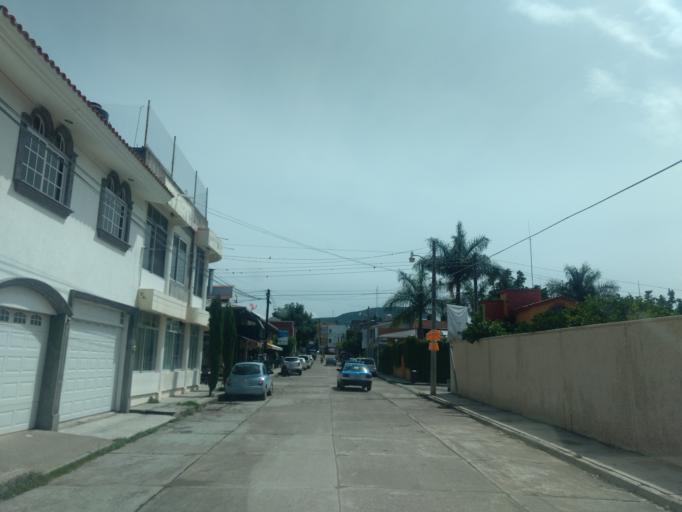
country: MX
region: Oaxaca
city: Ciudad de Huajuapam de Leon
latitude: 17.8023
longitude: -97.7774
